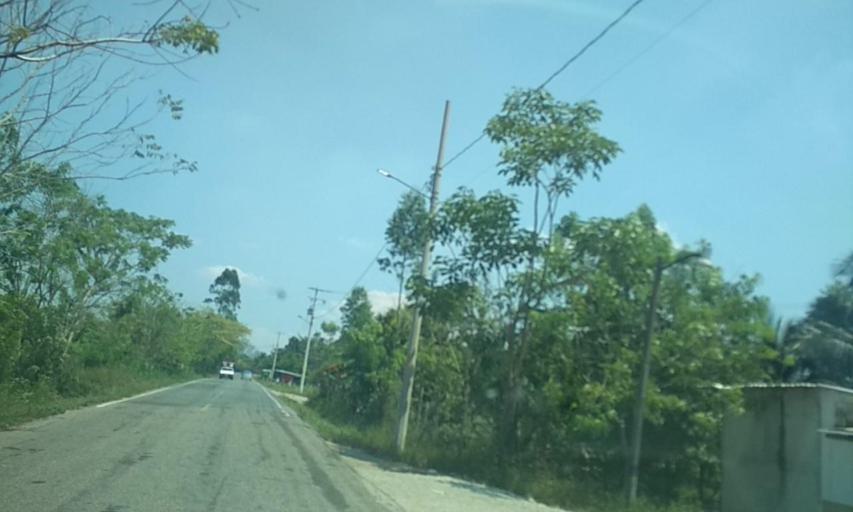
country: MX
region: Tabasco
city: Huimanguillo
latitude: 17.8041
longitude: -93.4923
